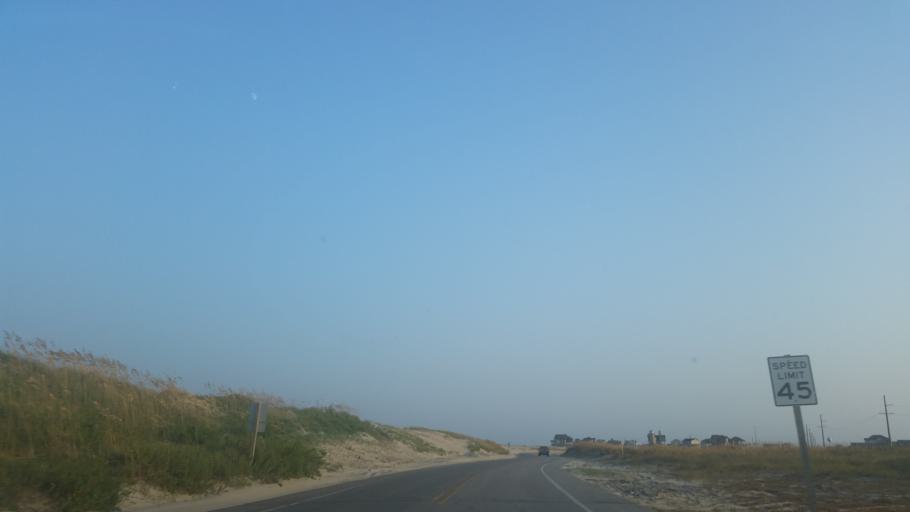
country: US
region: North Carolina
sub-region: Dare County
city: Wanchese
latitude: 35.6120
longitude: -75.4669
